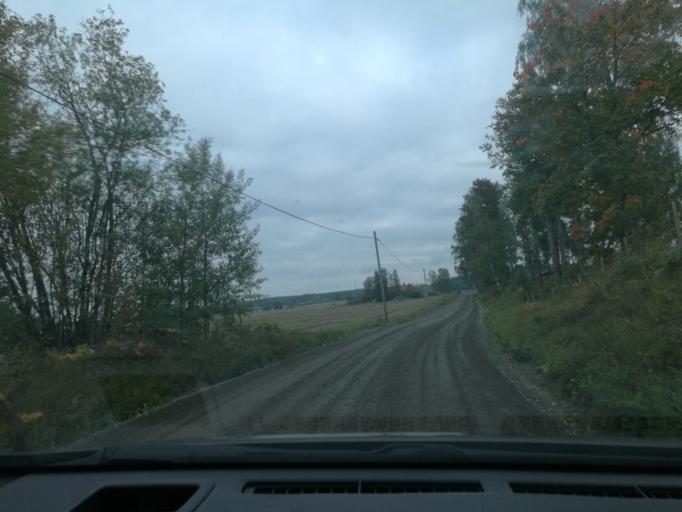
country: SE
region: Vaestmanland
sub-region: Vasteras
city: Tillberga
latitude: 59.7386
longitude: 16.7014
